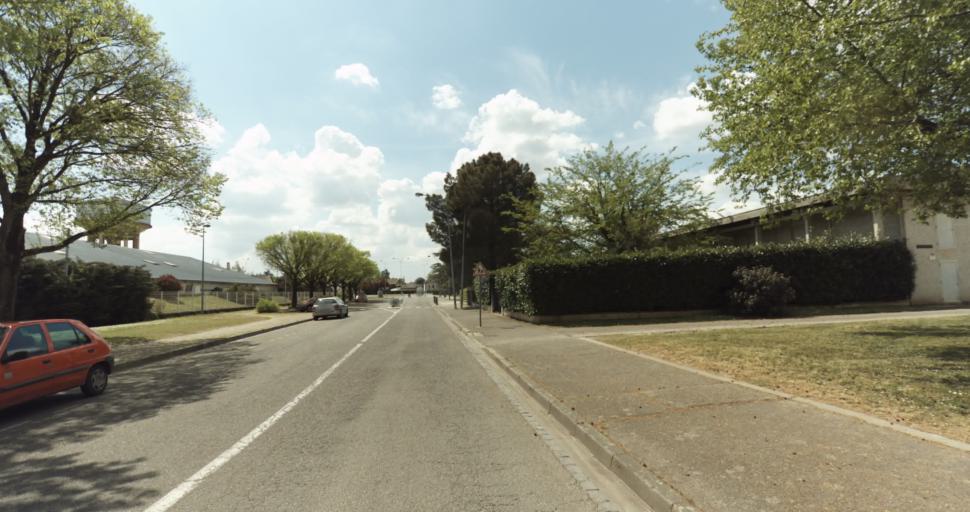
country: FR
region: Aquitaine
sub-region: Departement du Lot-et-Garonne
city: Agen
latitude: 44.1954
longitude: 0.6319
